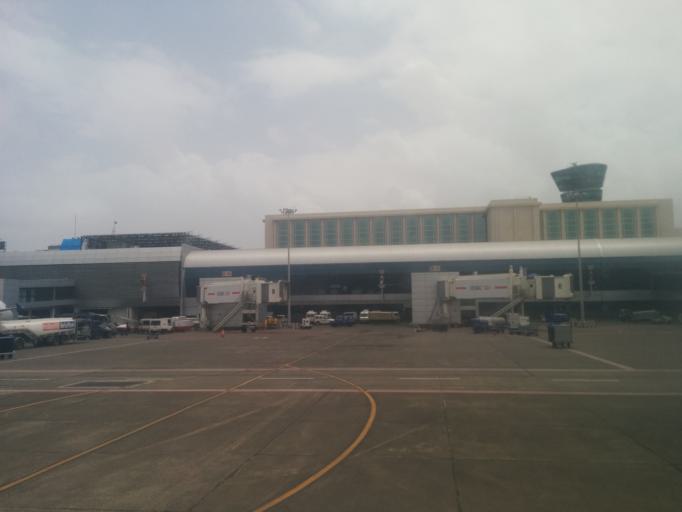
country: IN
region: Maharashtra
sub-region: Mumbai Suburban
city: Mumbai
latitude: 19.0910
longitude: 72.8541
